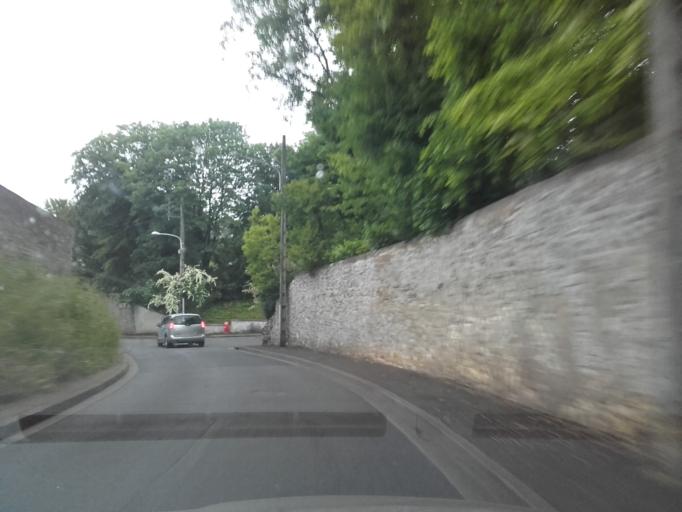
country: FR
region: Centre
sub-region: Departement d'Indre-et-Loire
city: Tours
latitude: 47.4059
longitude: 0.6918
